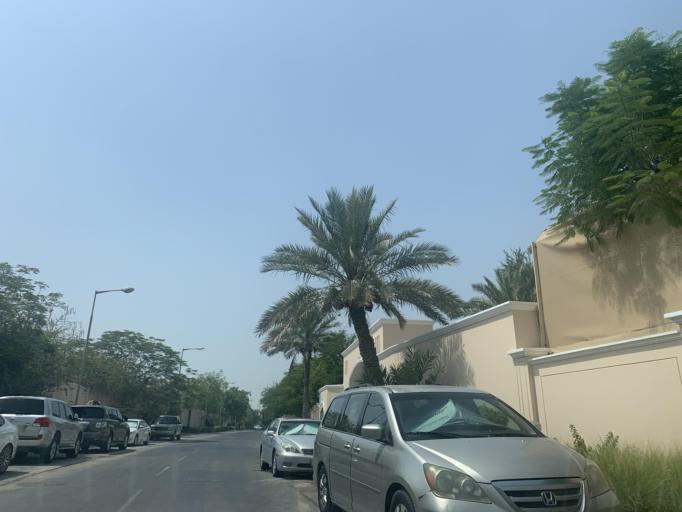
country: BH
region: Manama
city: Jidd Hafs
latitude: 26.1998
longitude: 50.4943
